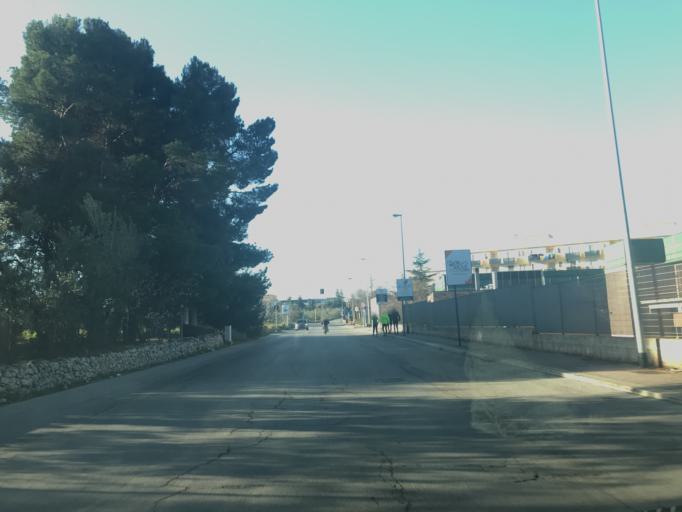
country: IT
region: Apulia
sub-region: Provincia di Bari
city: Corato
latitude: 41.1399
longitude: 16.4155
